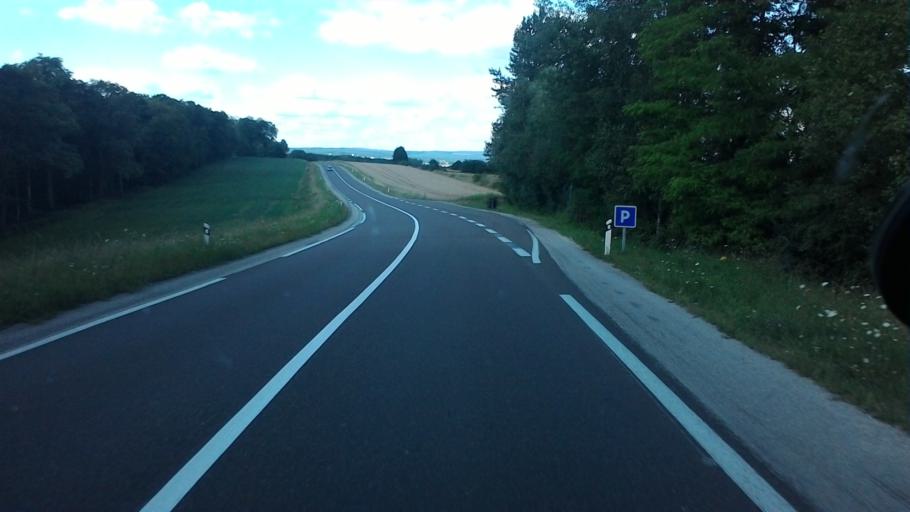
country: FR
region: Franche-Comte
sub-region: Departement de la Haute-Saone
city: Luxeuil-les-Bains
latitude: 47.7563
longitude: 6.3369
